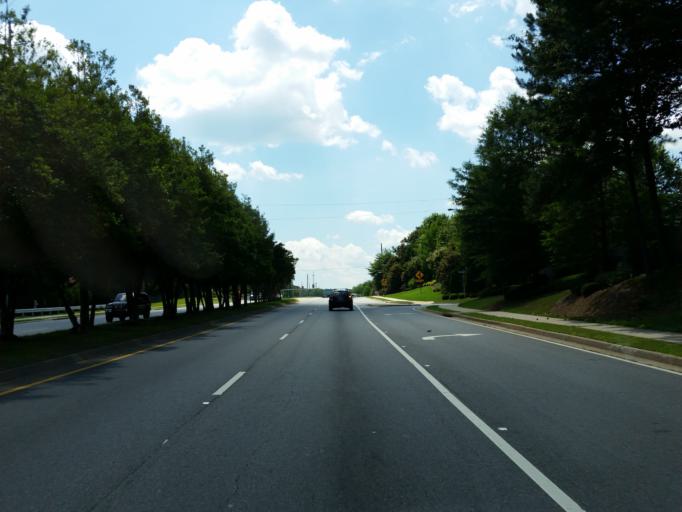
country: US
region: Georgia
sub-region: Cobb County
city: Marietta
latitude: 33.9746
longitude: -84.4758
